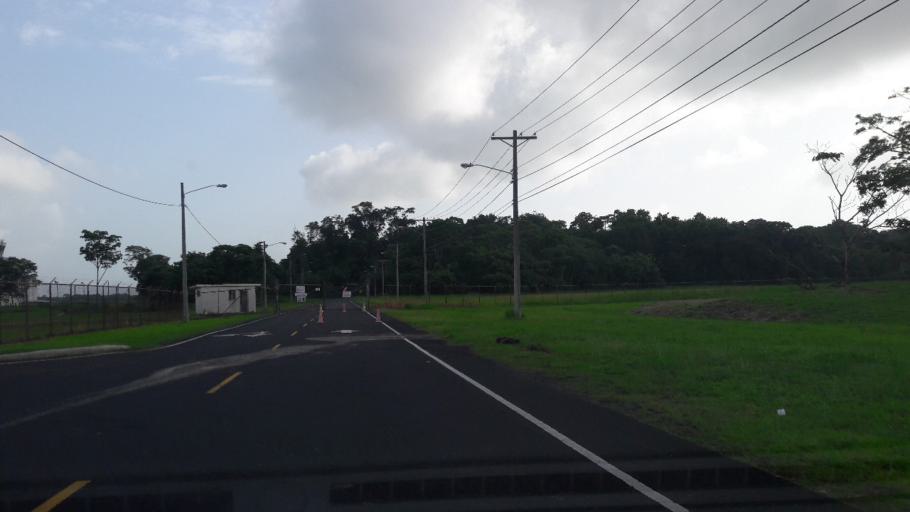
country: PA
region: Colon
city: Cativa
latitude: 9.3611
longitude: -79.8631
